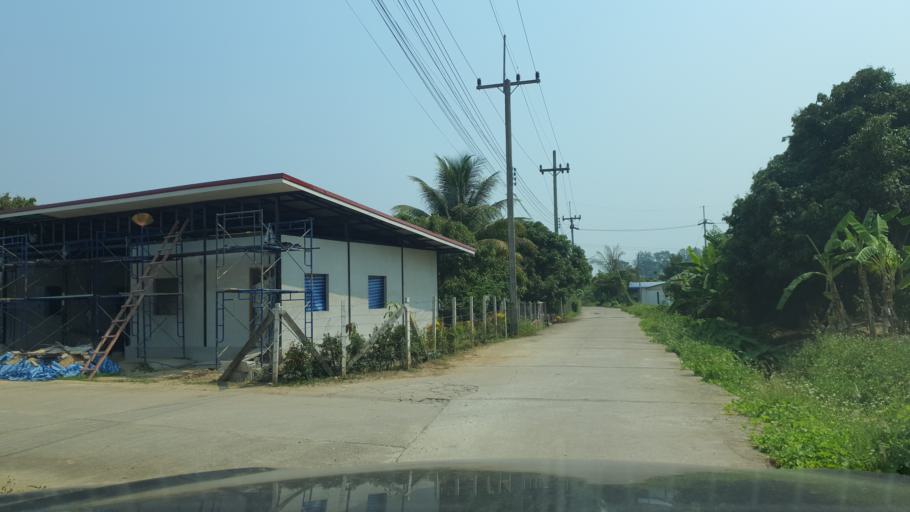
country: TH
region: Chiang Mai
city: Saraphi
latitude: 18.6708
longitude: 98.9882
